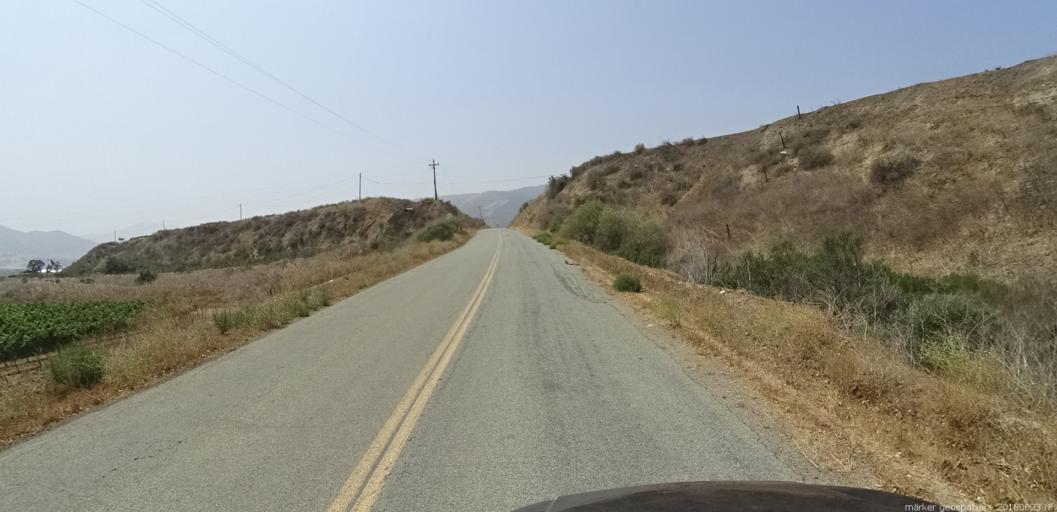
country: US
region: California
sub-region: Monterey County
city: Greenfield
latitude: 36.3190
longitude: -121.3021
